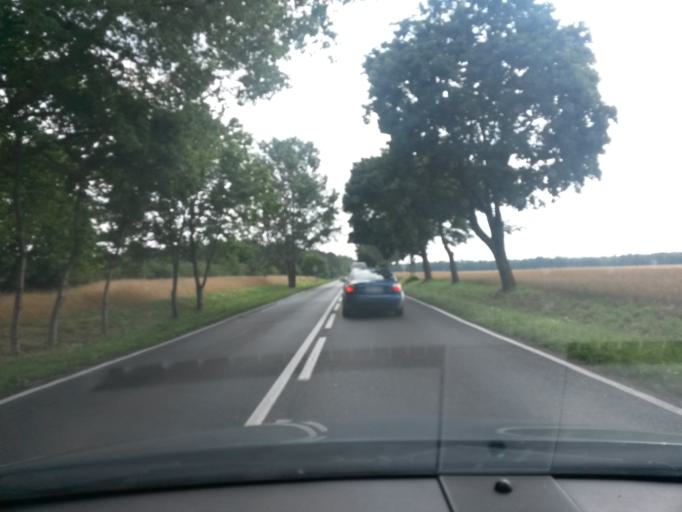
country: PL
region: Greater Poland Voivodeship
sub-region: Powiat poznanski
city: Kornik
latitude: 52.1799
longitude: 17.0509
